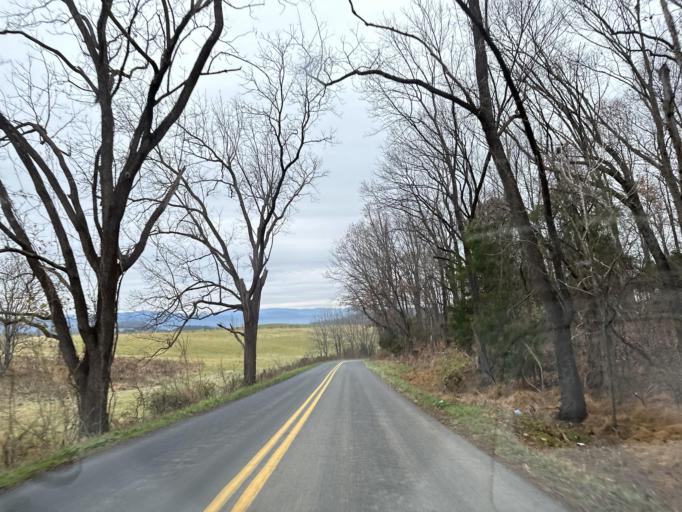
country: US
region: Virginia
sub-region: Rockingham County
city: Bridgewater
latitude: 38.3306
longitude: -79.0785
